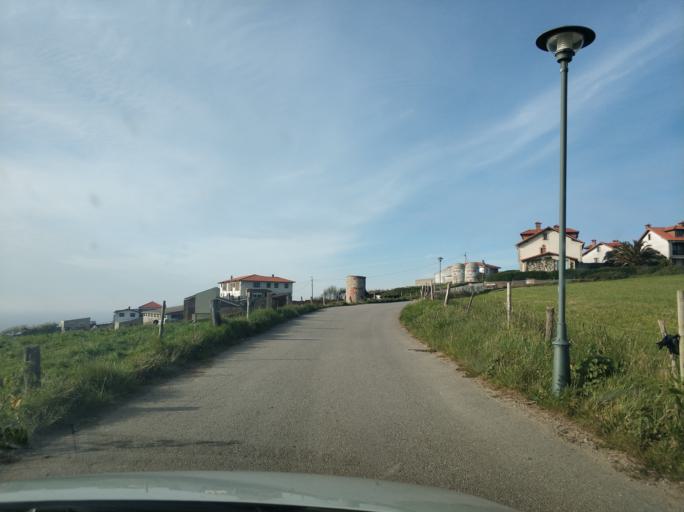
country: ES
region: Cantabria
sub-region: Provincia de Cantabria
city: San Vicente de la Barquera
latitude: 43.3976
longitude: -4.3506
